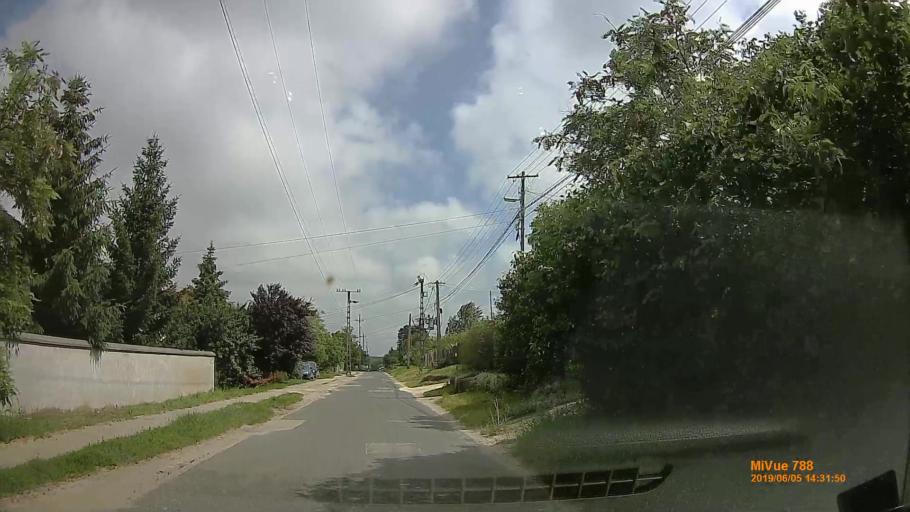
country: HU
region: Pest
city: Kistarcsa
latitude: 47.5581
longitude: 19.2659
